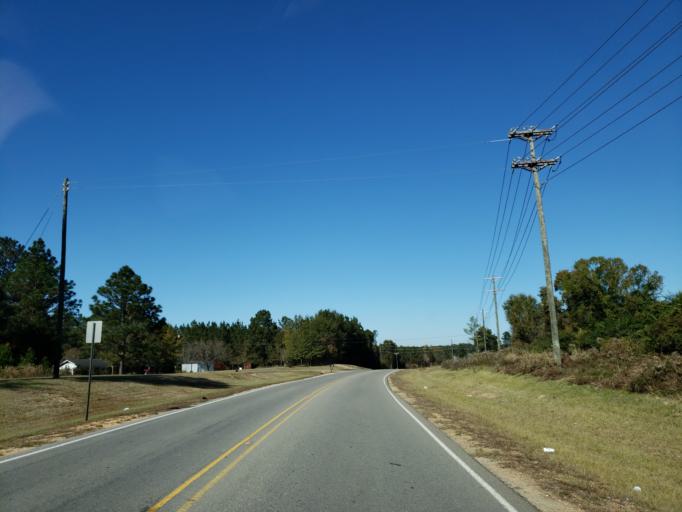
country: US
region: Mississippi
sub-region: Lamar County
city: West Hattiesburg
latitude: 31.3268
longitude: -89.3999
